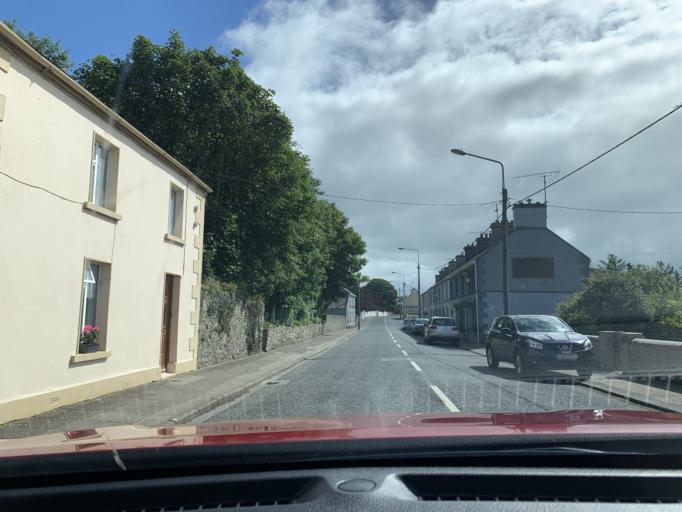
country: IE
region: Connaught
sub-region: County Leitrim
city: Carrick-on-Shannon
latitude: 53.8461
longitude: -8.1991
